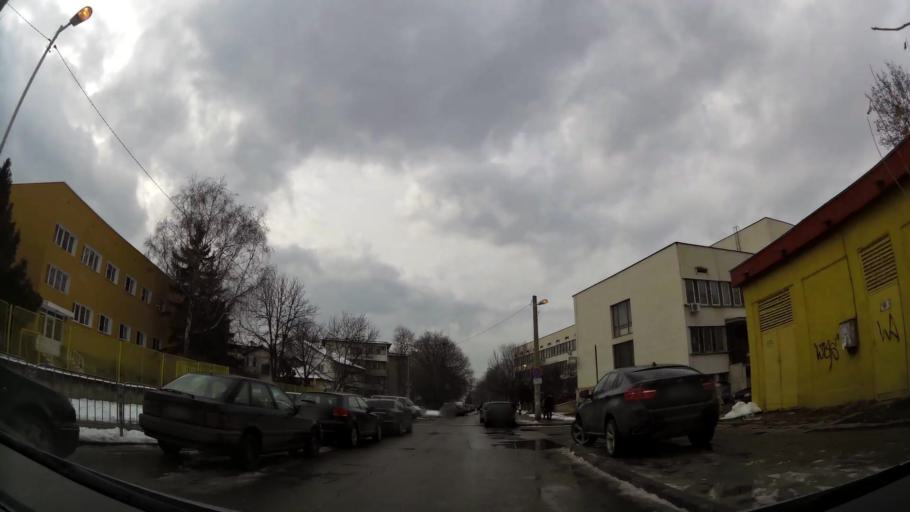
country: BG
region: Sofia-Capital
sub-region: Stolichna Obshtina
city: Sofia
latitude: 42.7015
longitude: 23.3698
